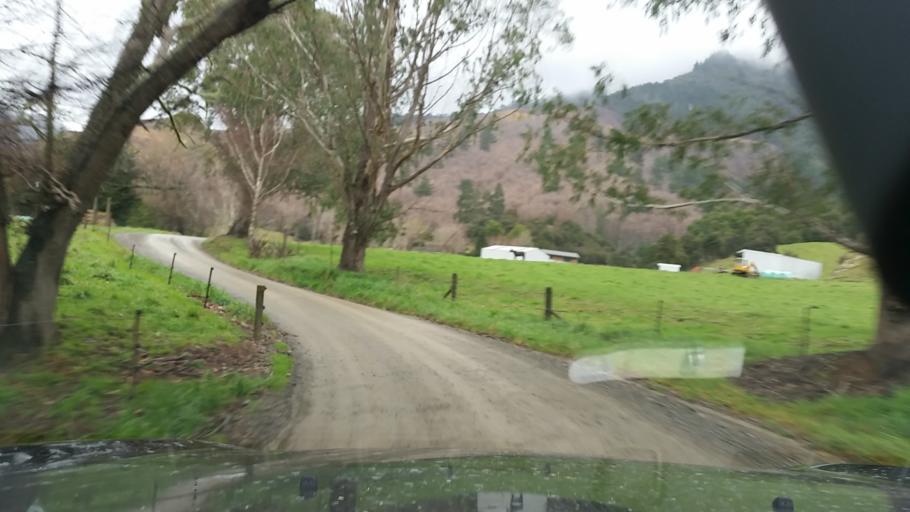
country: NZ
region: Marlborough
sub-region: Marlborough District
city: Picton
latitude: -41.3022
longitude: 173.6634
